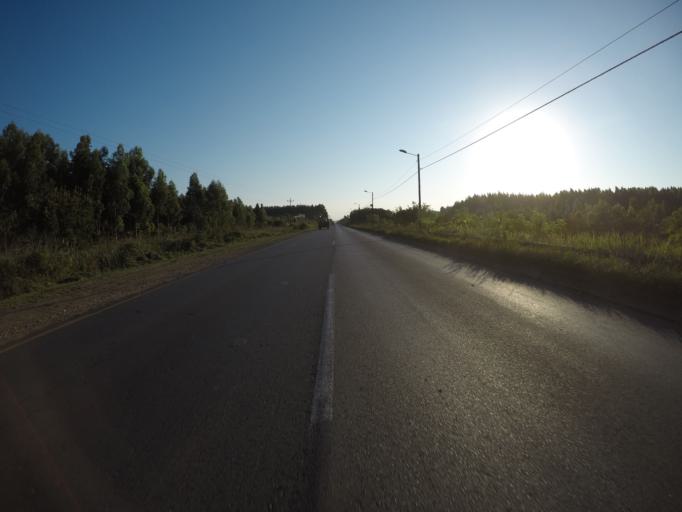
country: ZA
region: KwaZulu-Natal
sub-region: uThungulu District Municipality
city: KwaMbonambi
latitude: -28.6831
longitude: 32.1959
